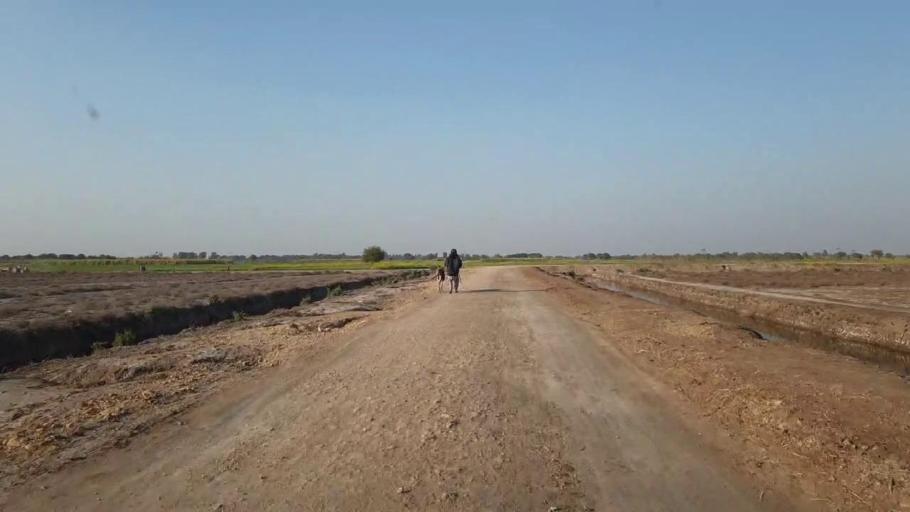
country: PK
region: Sindh
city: Chambar
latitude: 25.3396
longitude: 68.7017
